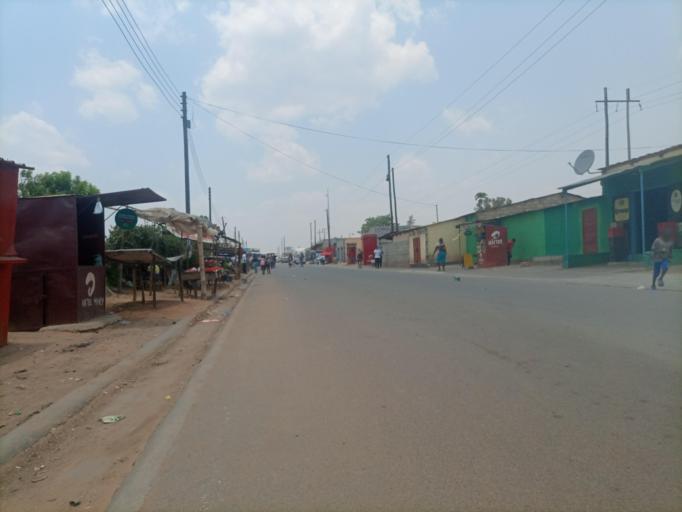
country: ZM
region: Lusaka
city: Lusaka
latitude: -15.4050
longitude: 28.3697
